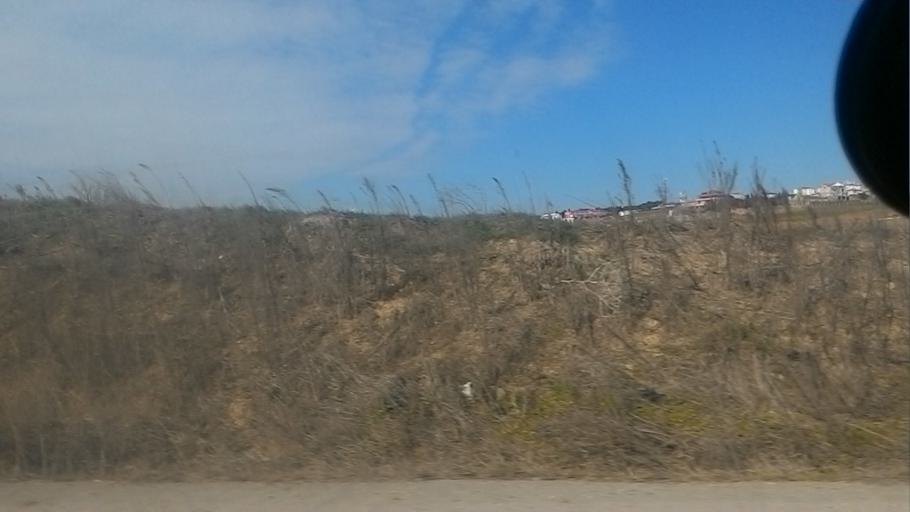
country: TR
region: Istanbul
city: Canta
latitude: 41.0771
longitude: 28.0752
